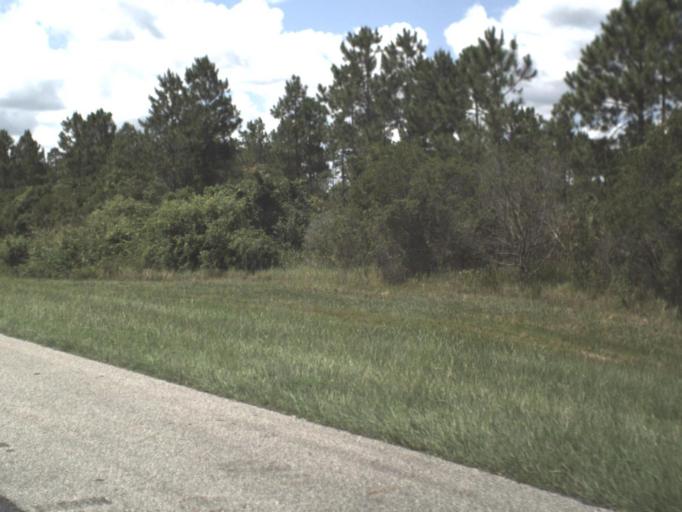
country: US
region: Florida
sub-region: Saint Johns County
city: Saint Augustine Shores
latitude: 29.7385
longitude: -81.3429
